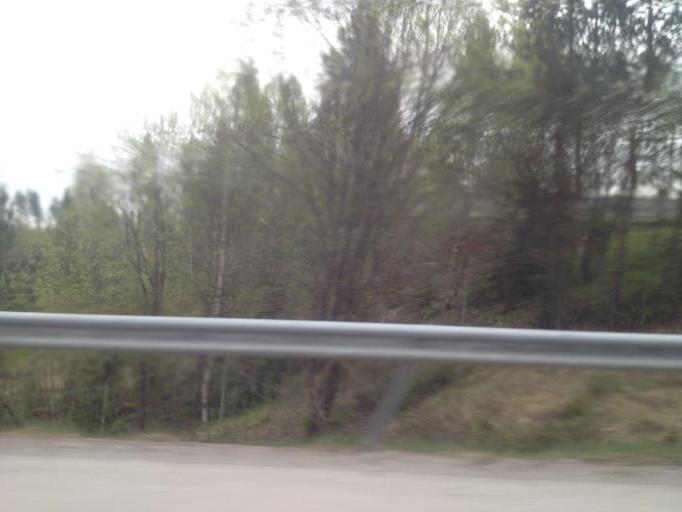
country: FI
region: Uusimaa
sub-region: Helsinki
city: Nurmijaervi
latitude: 60.4288
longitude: 24.8278
